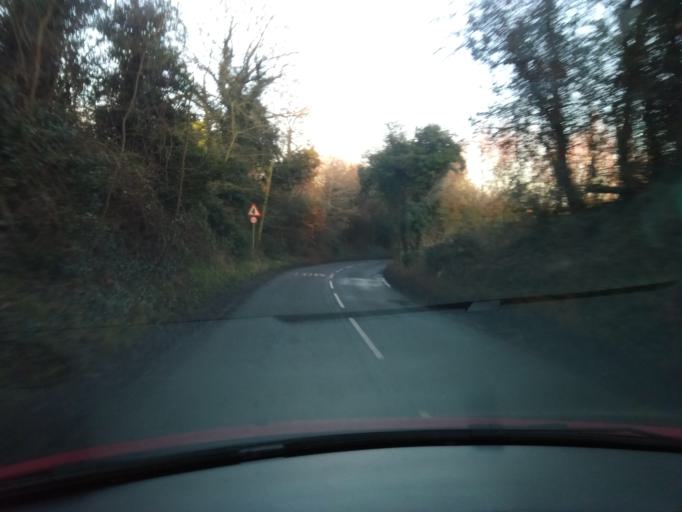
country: GB
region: England
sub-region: Leicestershire
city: Barrow upon Soar
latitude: 52.7703
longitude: -1.1222
